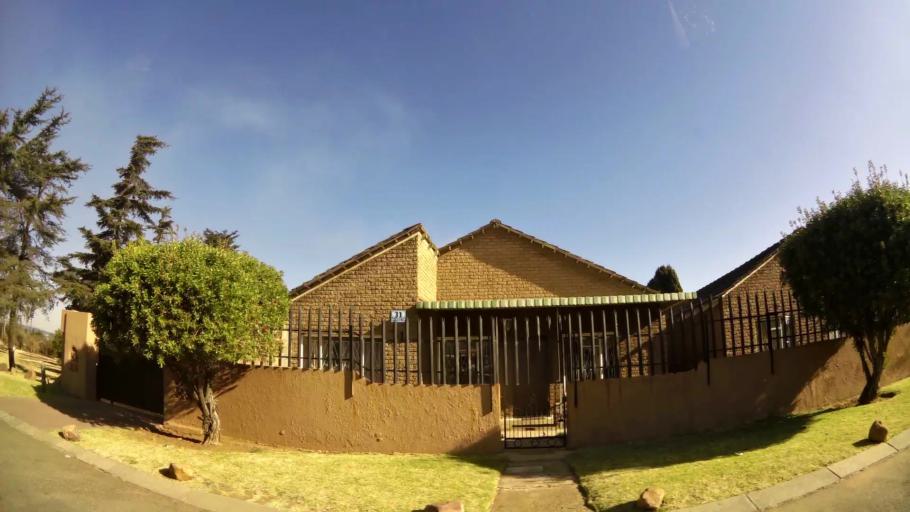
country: ZA
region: Gauteng
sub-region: City of Johannesburg Metropolitan Municipality
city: Johannesburg
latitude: -26.2103
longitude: 27.9744
